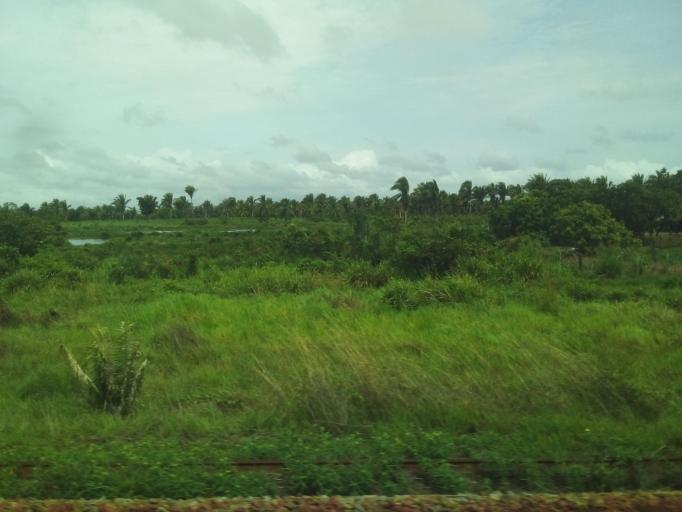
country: BR
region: Maranhao
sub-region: Arari
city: Arari
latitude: -3.5185
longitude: -44.6299
